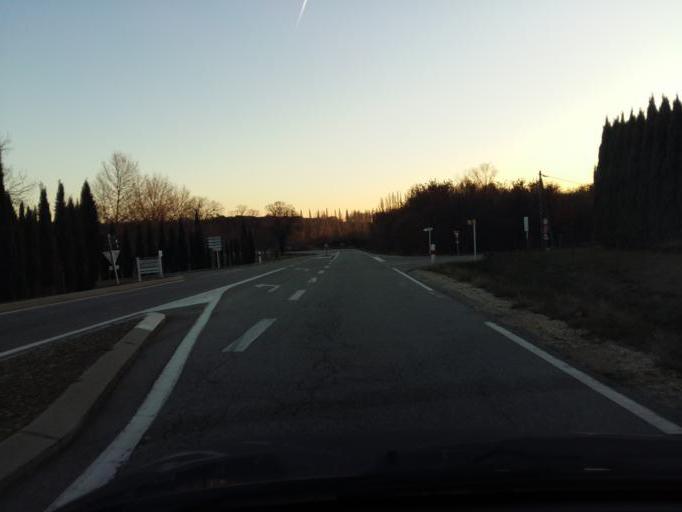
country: FR
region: Rhone-Alpes
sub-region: Departement de la Drome
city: Grignan
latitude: 44.4176
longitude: 4.9017
